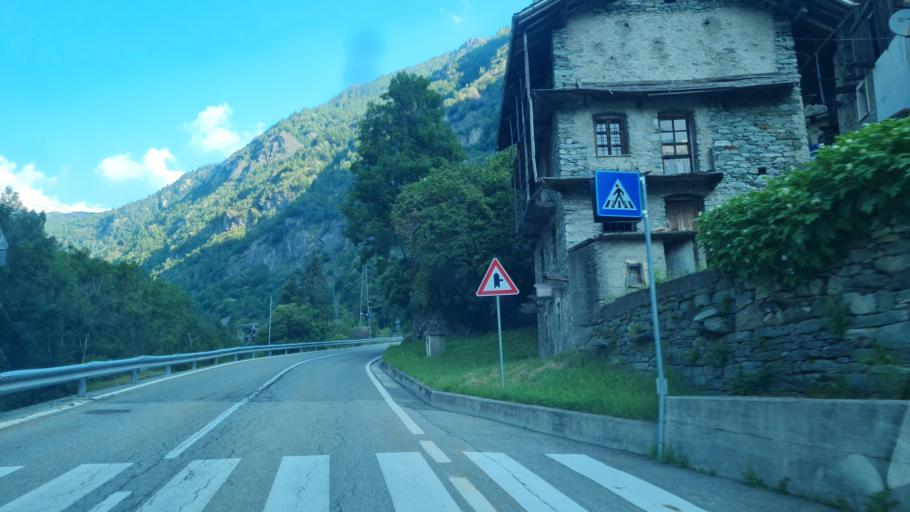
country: IT
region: Aosta Valley
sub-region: Valle d'Aosta
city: Pont-Bozet
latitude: 45.6126
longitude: 7.6806
